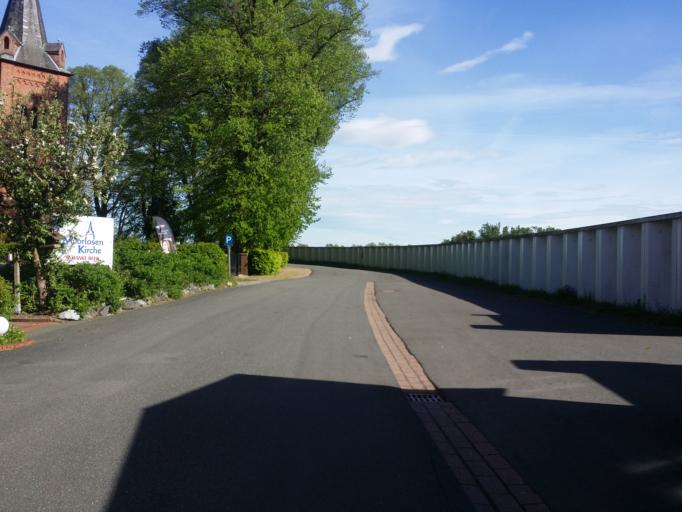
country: DE
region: Lower Saxony
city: Lemwerder
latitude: 53.1287
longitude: 8.6531
